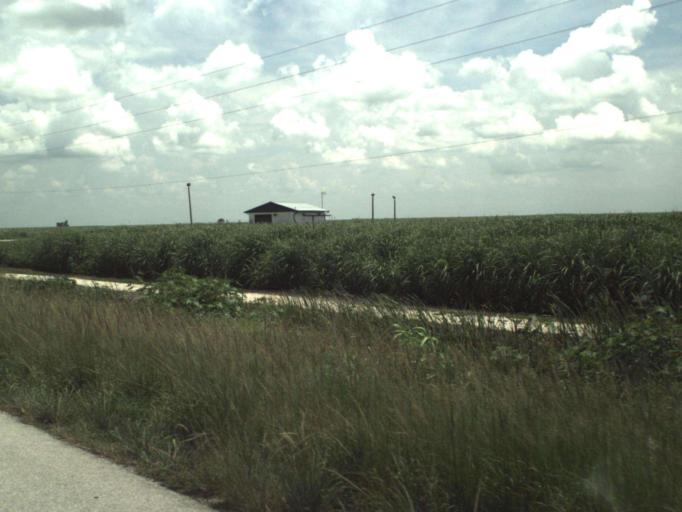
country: US
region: Florida
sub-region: Palm Beach County
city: Pahokee
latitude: 26.8284
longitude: -80.5841
